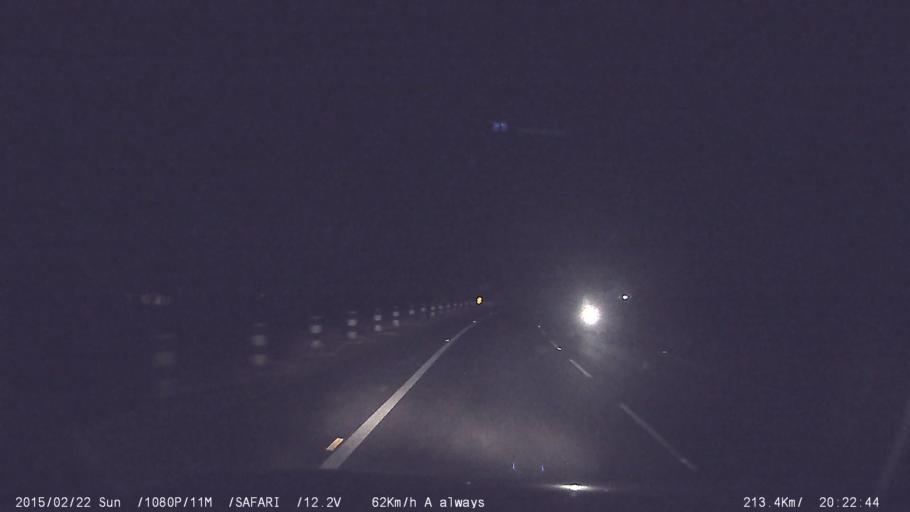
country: IN
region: Tamil Nadu
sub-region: Dindigul
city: Dindigul
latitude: 10.2975
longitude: 77.8821
